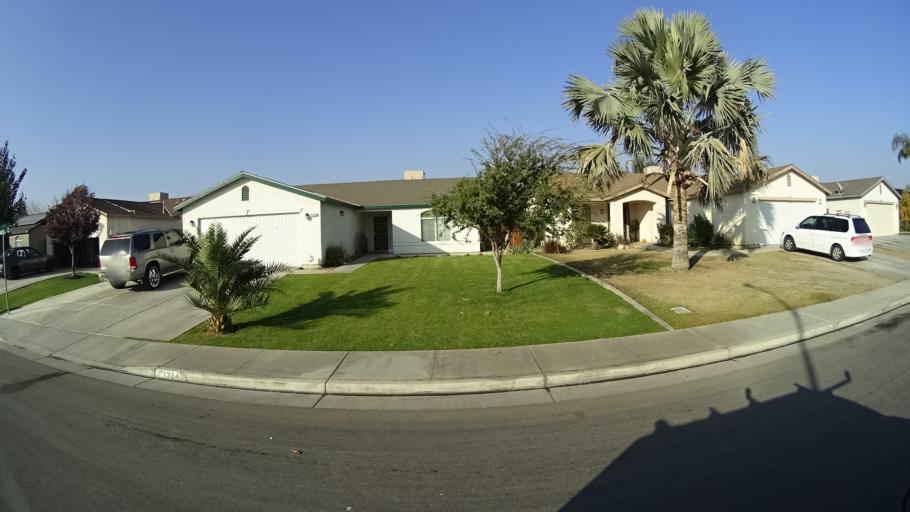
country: US
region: California
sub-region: Kern County
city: Greenfield
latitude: 35.2862
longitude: -119.0177
